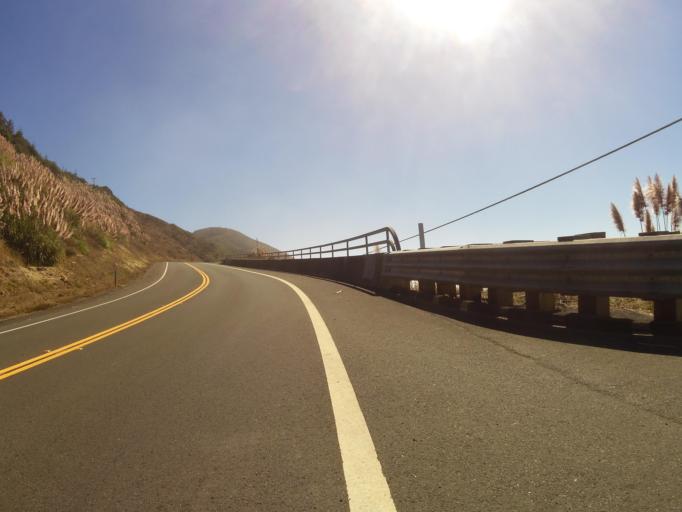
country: US
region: California
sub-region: Mendocino County
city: Fort Bragg
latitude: 39.6109
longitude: -123.7826
